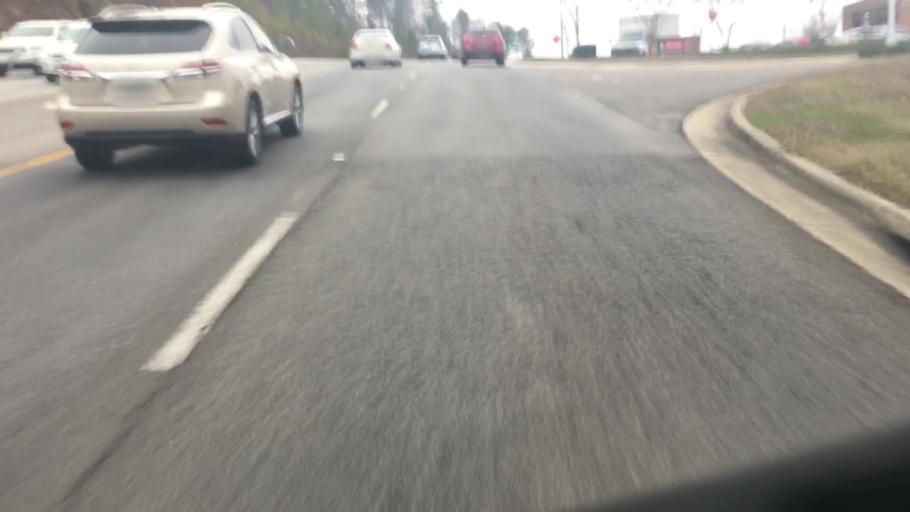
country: US
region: Alabama
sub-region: Shelby County
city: Helena
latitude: 33.3558
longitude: -86.8594
